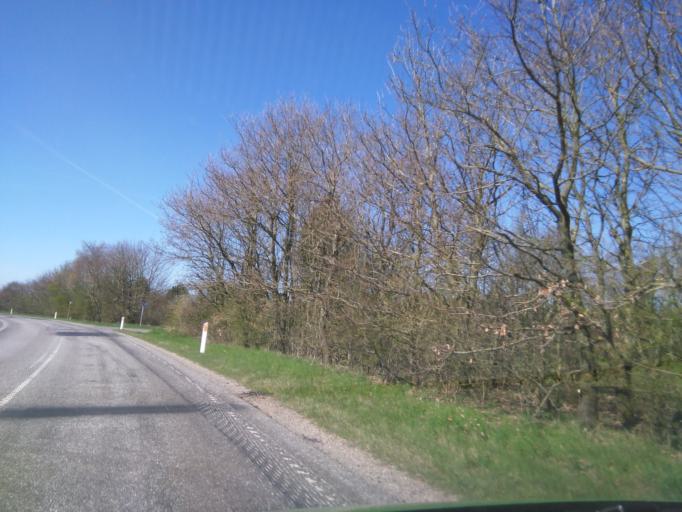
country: DK
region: South Denmark
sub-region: Billund Kommune
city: Billund
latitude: 55.7082
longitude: 9.0285
